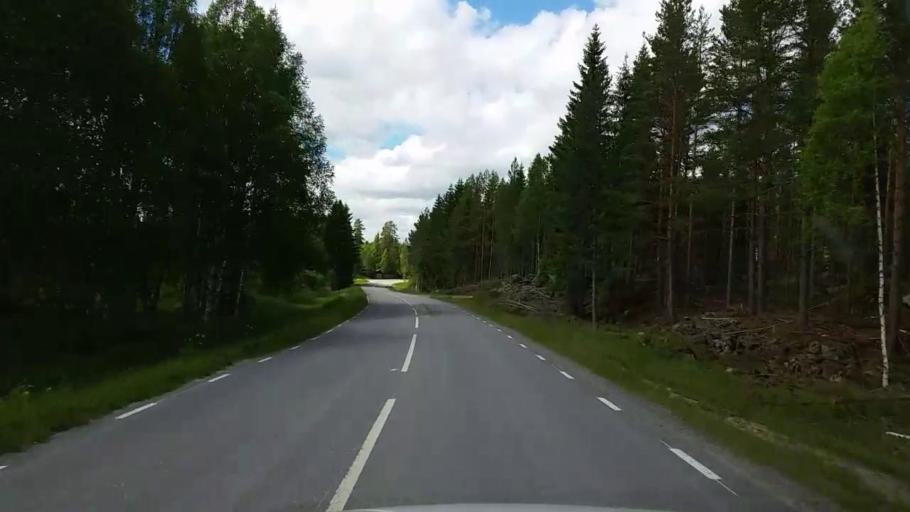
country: SE
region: Gaevleborg
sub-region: Bollnas Kommun
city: Vittsjo
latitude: 61.0630
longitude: 16.3146
